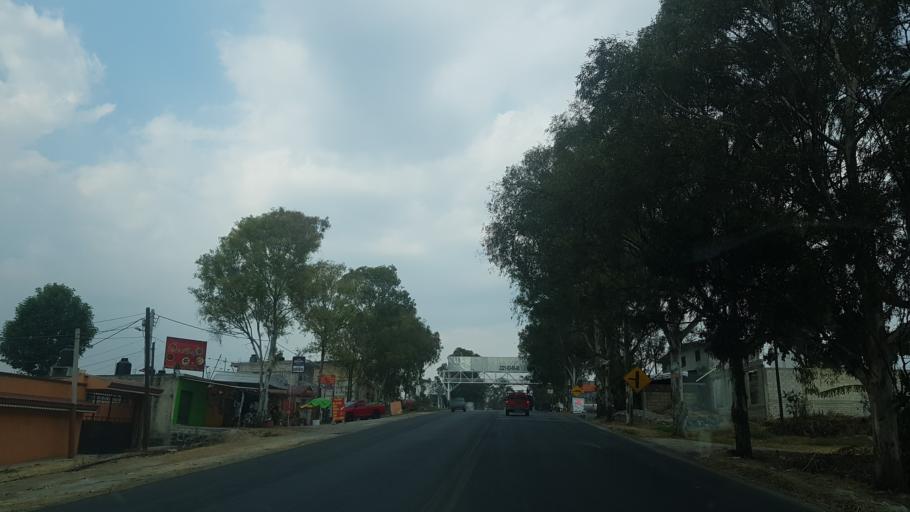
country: MX
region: Puebla
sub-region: Santa Isabel Cholula
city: San Pablo Ahuatempa
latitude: 18.9837
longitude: -98.3658
